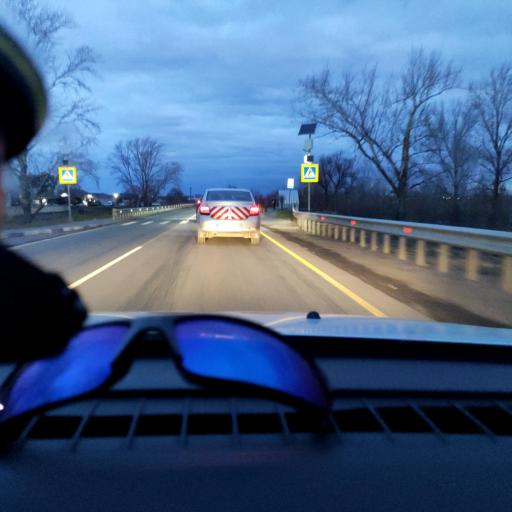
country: RU
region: Samara
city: Samara
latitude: 53.1169
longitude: 50.1234
